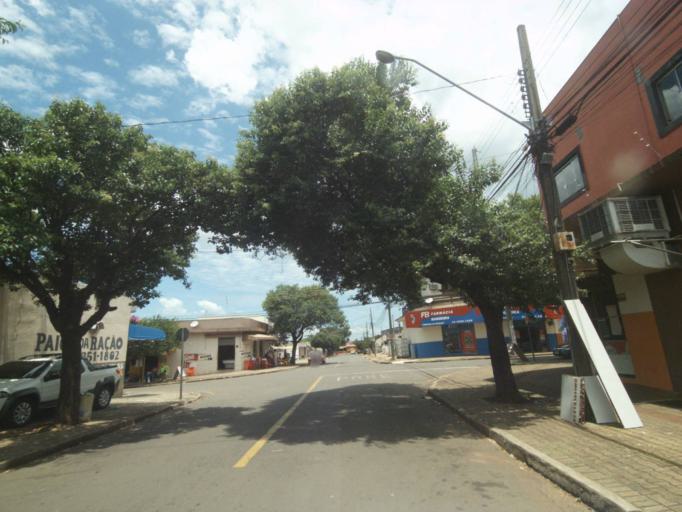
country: BR
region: Parana
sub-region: Londrina
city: Londrina
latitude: -23.3103
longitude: -51.2171
